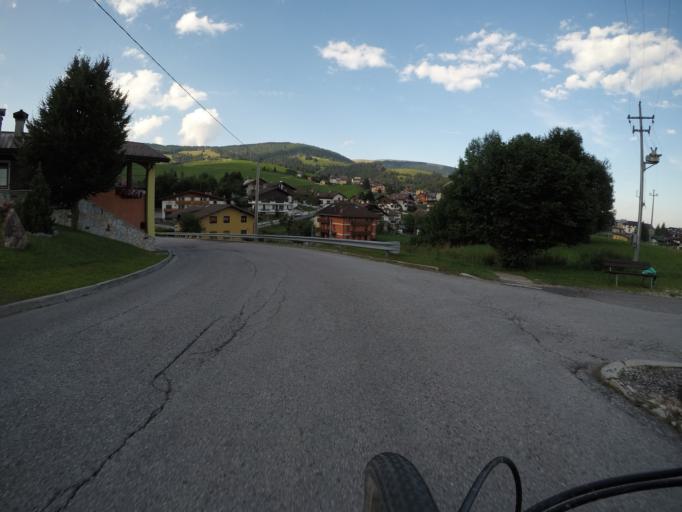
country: IT
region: Veneto
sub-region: Provincia di Vicenza
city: Gallio
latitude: 45.8927
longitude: 11.5412
